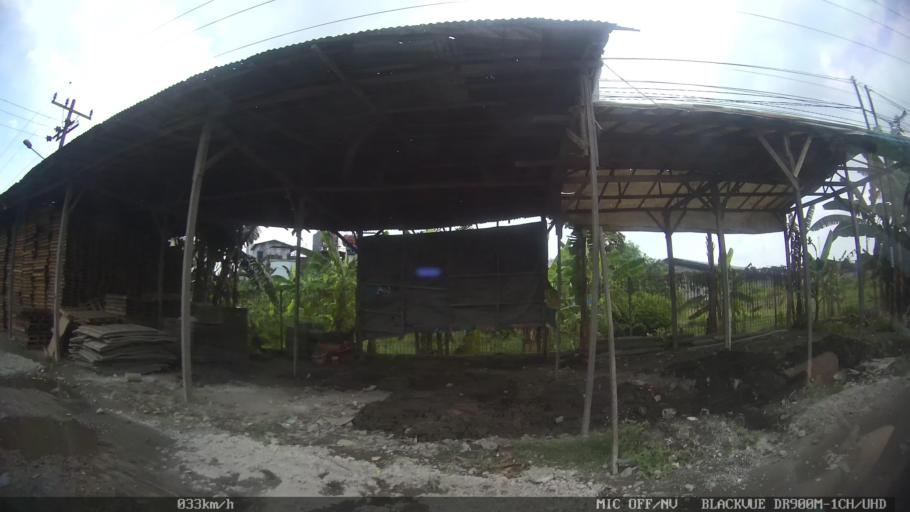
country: ID
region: North Sumatra
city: Labuhan Deli
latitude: 3.6754
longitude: 98.6742
